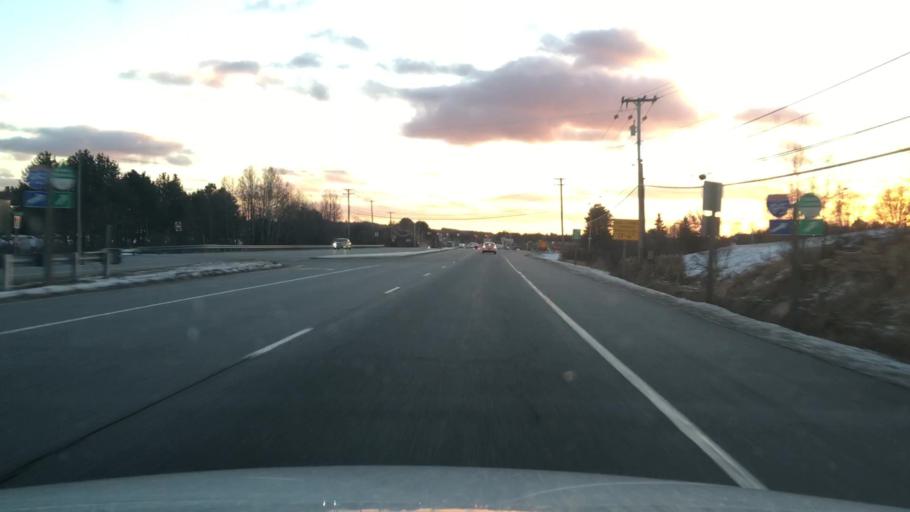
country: US
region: Maine
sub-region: Androscoggin County
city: Auburn
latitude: 44.0388
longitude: -70.2634
